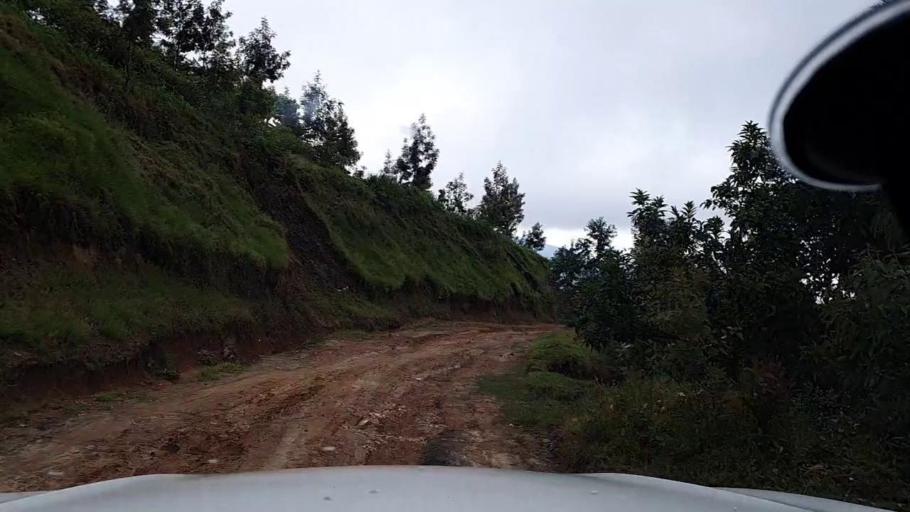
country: RW
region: Western Province
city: Kibuye
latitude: -2.0871
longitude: 29.4998
